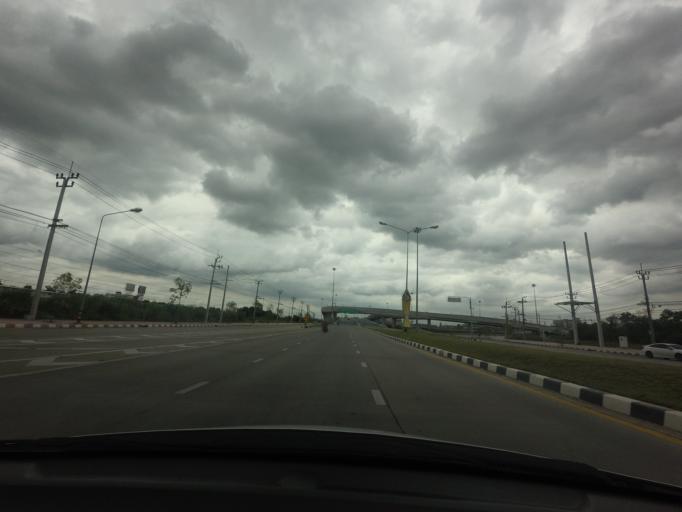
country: TH
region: Bangkok
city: Lat Krabang
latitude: 13.7561
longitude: 100.7426
